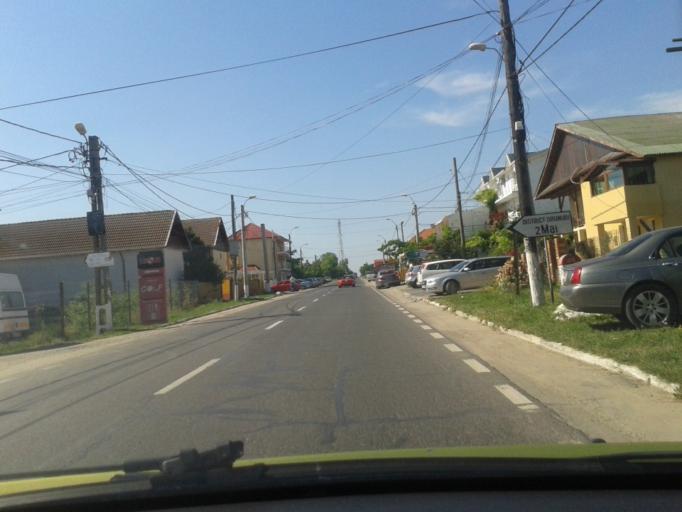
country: RO
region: Constanta
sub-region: Municipiul Mangalia
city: Mangalia
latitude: 43.7828
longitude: 28.5781
